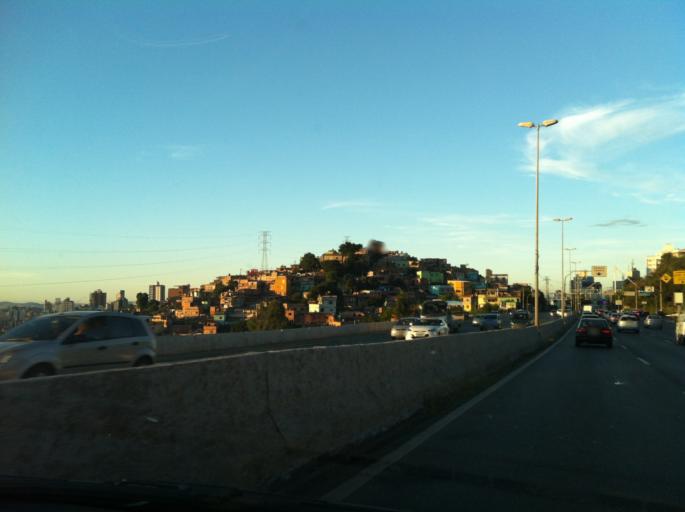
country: BR
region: Minas Gerais
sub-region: Belo Horizonte
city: Belo Horizonte
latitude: -19.9593
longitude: -43.9434
